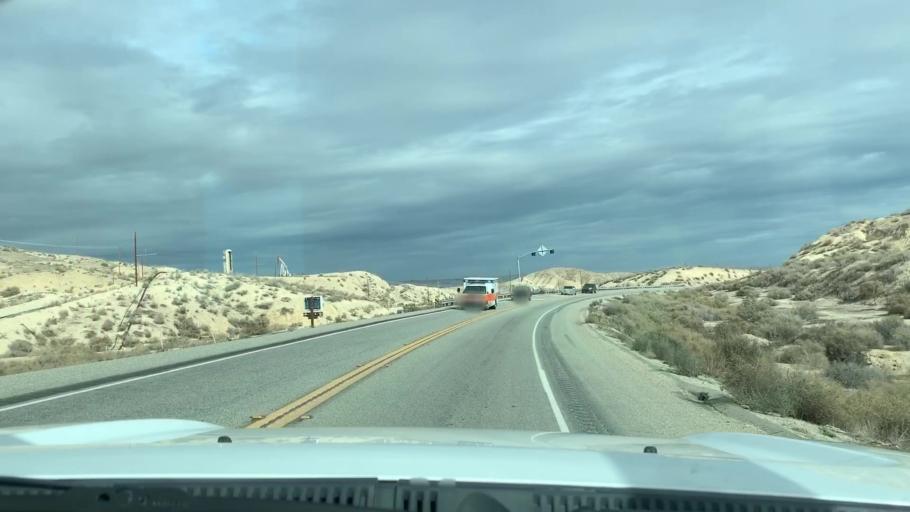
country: US
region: California
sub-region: Kern County
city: Ford City
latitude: 35.1825
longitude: -119.4536
